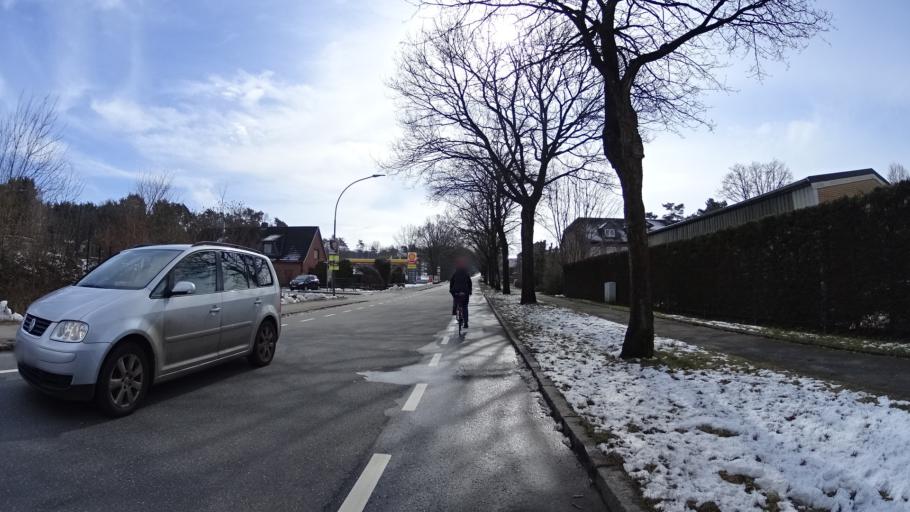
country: DE
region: Schleswig-Holstein
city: Boostedt
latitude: 54.0145
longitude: 10.0195
